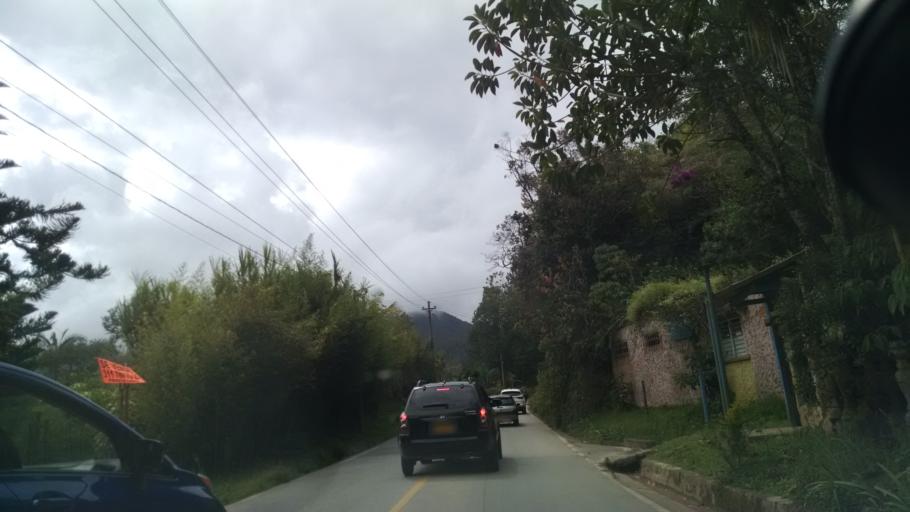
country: CO
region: Antioquia
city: Guatape
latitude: 6.2082
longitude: -75.2201
